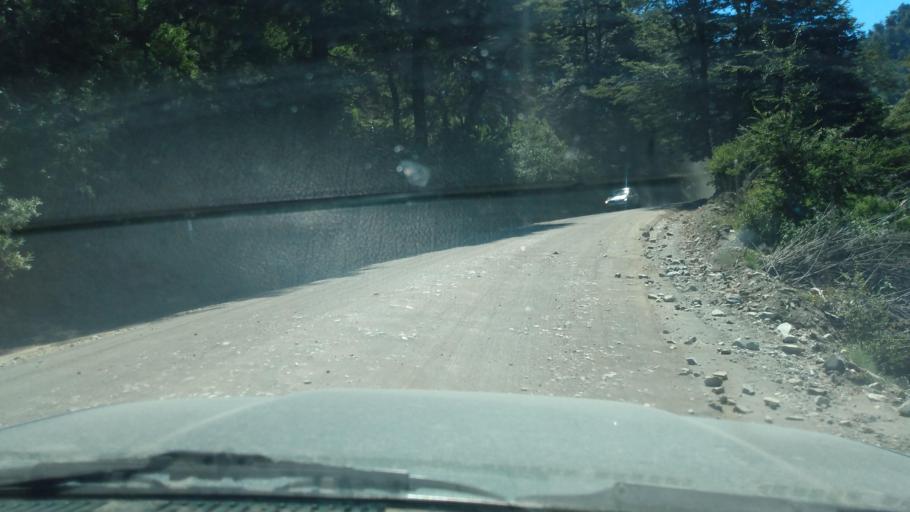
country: AR
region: Neuquen
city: Villa La Angostura
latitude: -40.6050
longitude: -71.6191
